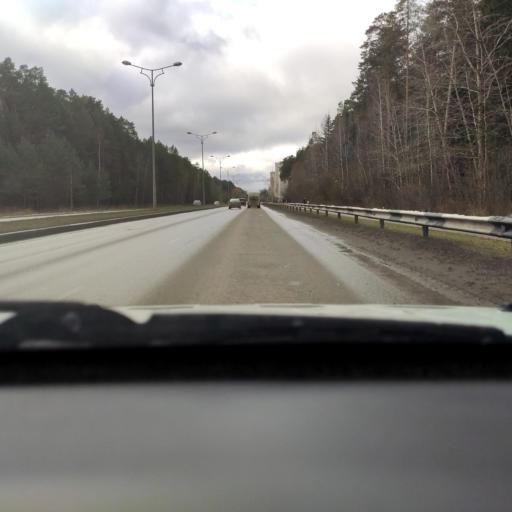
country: RU
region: Perm
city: Kondratovo
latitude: 58.0183
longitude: 55.9894
